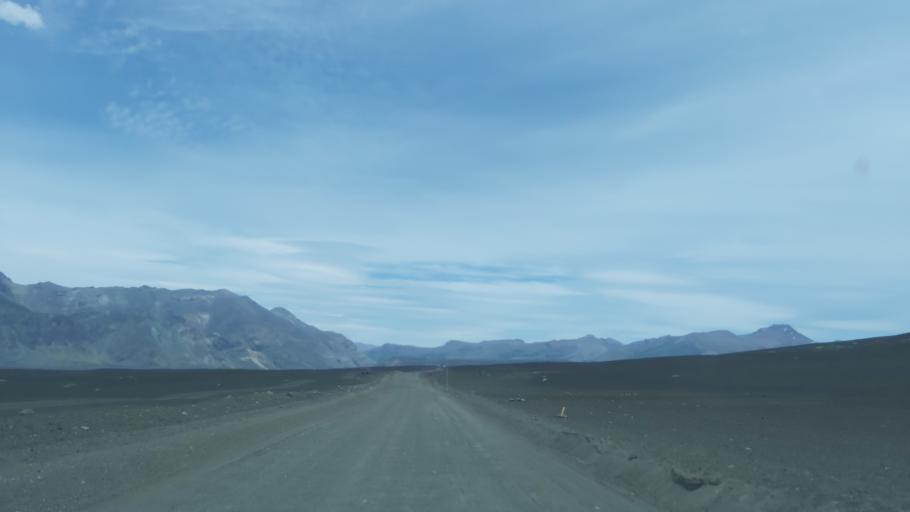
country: AR
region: Neuquen
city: Andacollo
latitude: -37.4263
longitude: -71.2872
